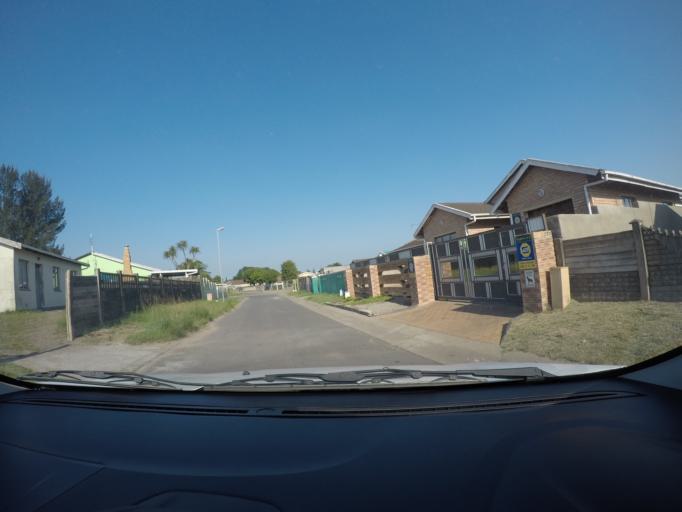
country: ZA
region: KwaZulu-Natal
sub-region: uThungulu District Municipality
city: Richards Bay
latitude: -28.7175
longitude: 32.0356
